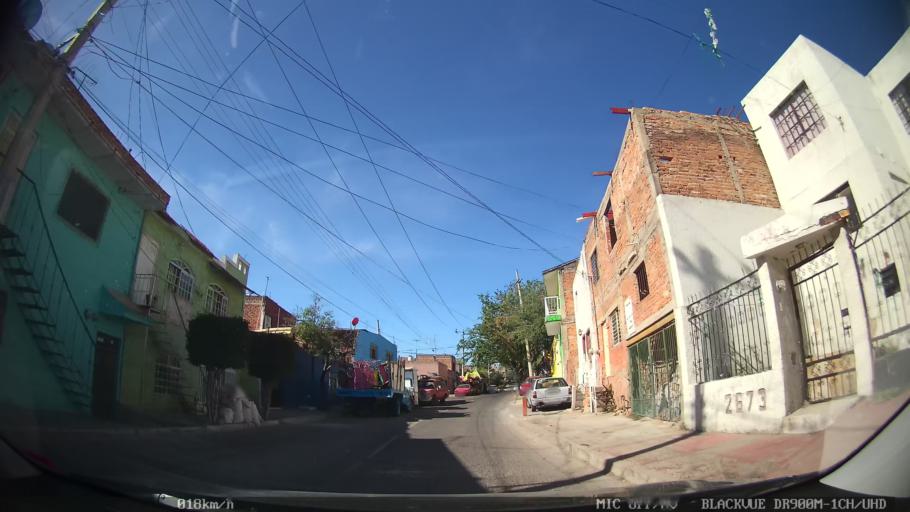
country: MX
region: Jalisco
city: Tlaquepaque
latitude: 20.6902
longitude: -103.2762
